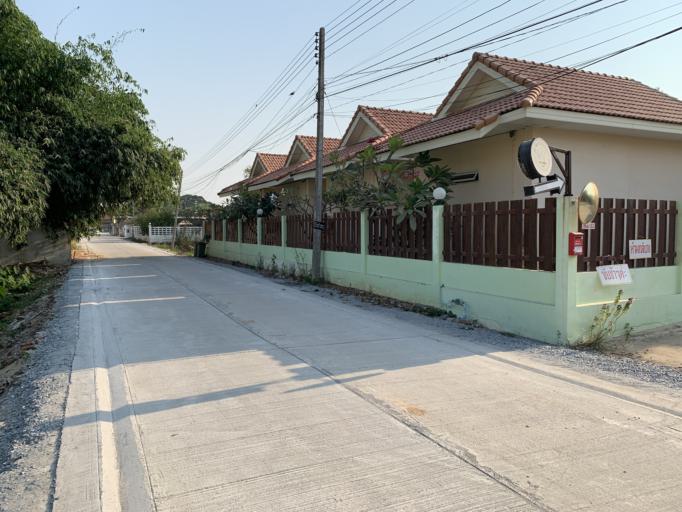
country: TH
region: Phitsanulok
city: Phitsanulok
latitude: 16.8158
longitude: 100.2911
